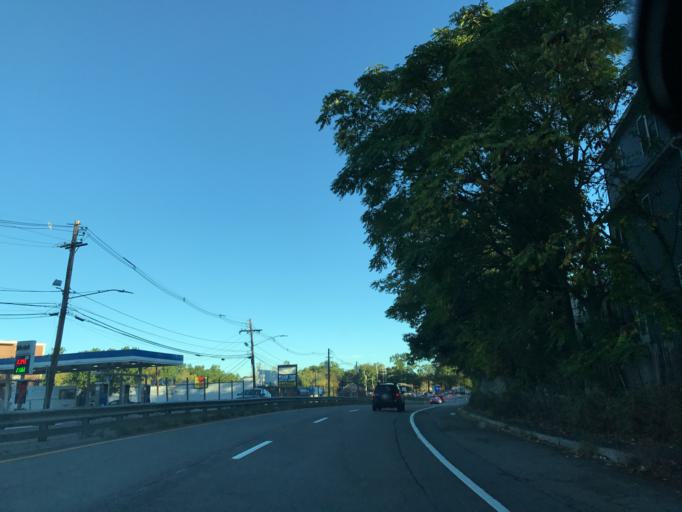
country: US
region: Massachusetts
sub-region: Norfolk County
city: Dedham
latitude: 42.2689
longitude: -71.1719
